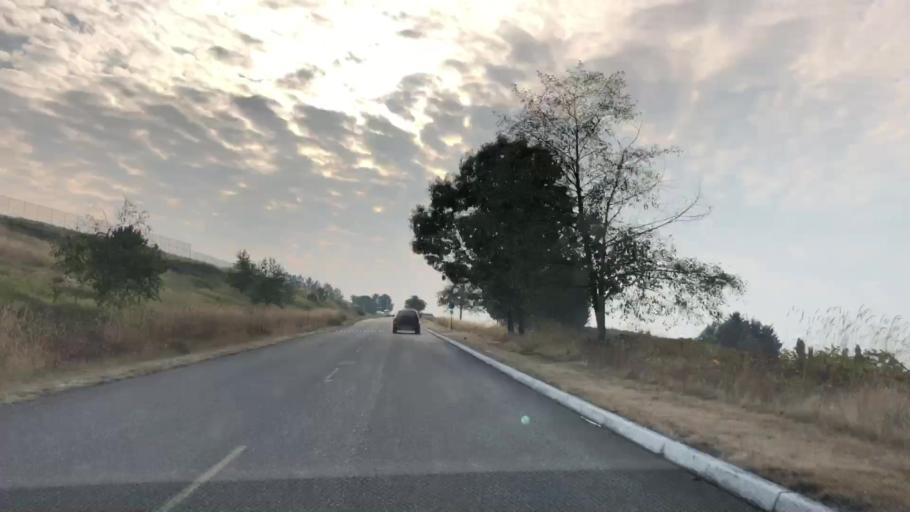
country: US
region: Washington
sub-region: King County
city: Newcastle
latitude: 47.5364
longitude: -122.1377
